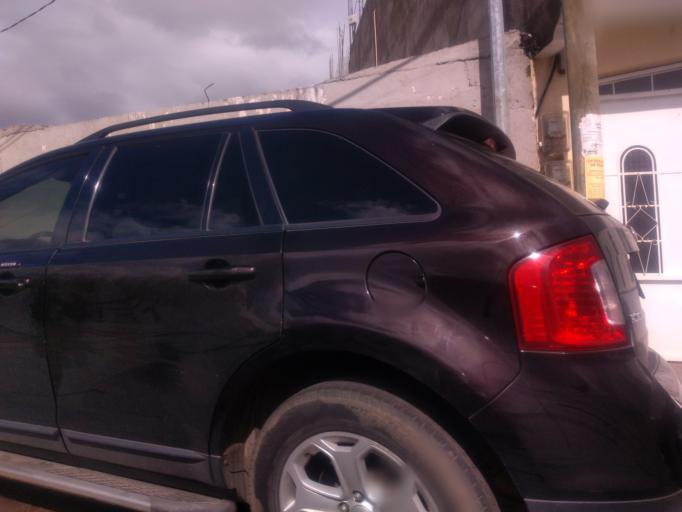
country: GT
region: Quetzaltenango
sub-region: Municipio de La Esperanza
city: La Esperanza
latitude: 14.8690
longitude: -91.5654
